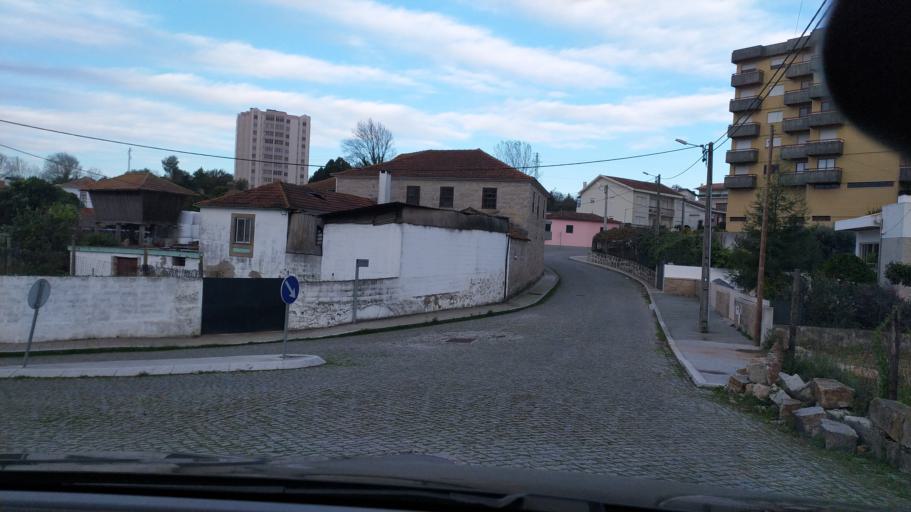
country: PT
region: Porto
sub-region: Maia
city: Gemunde
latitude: 41.2447
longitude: -8.6443
